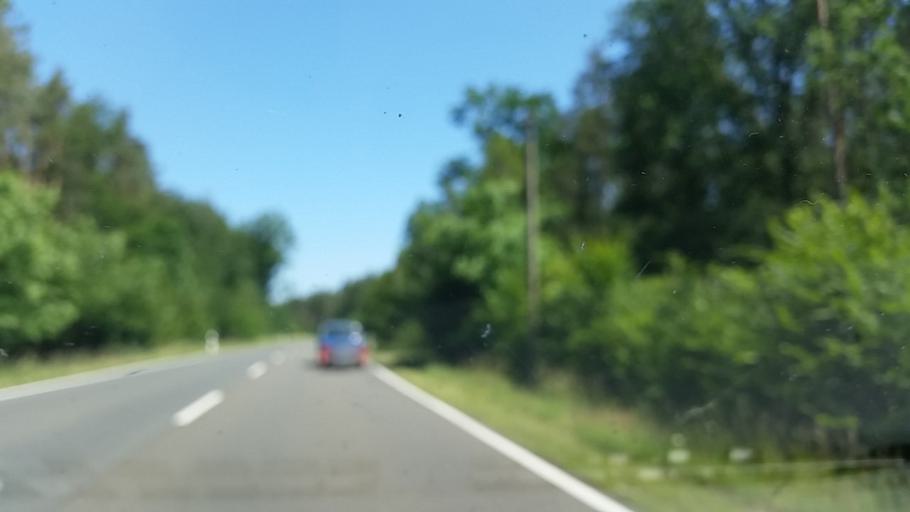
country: DE
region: Saxony-Anhalt
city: Kemberg
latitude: 51.7117
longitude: 12.6187
